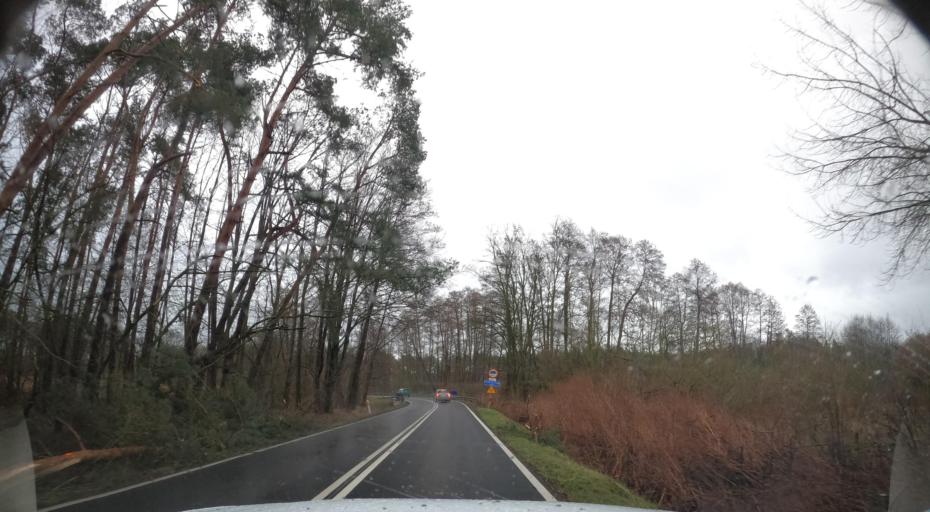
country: PL
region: West Pomeranian Voivodeship
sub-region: Powiat gryfinski
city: Stare Czarnowo
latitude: 53.3931
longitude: 14.7129
